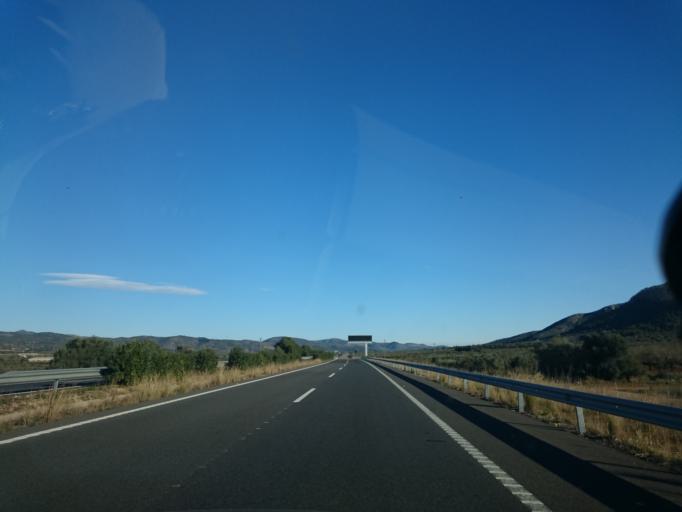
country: ES
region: Valencia
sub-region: Provincia de Castello
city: Alcala de Xivert
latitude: 40.2988
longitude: 0.2351
